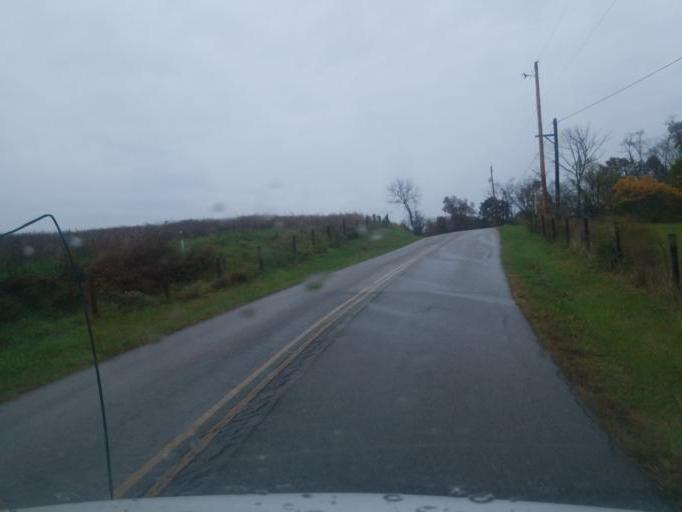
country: US
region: Ohio
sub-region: Washington County
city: Beverly
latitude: 39.4556
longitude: -81.6167
